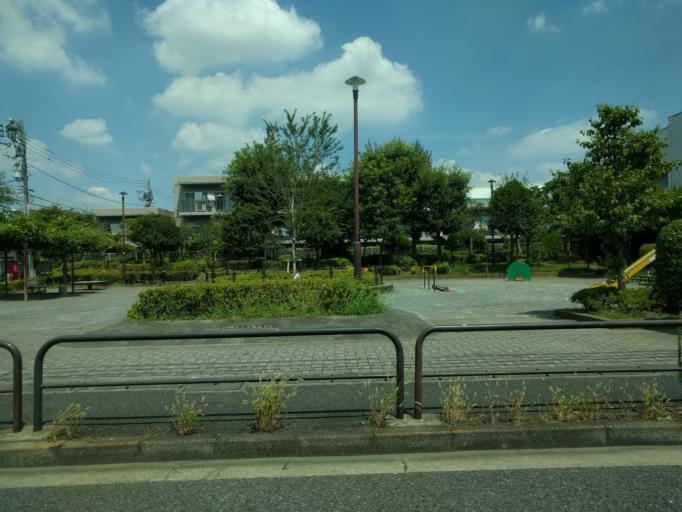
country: JP
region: Tokyo
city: Tokyo
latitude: 35.6301
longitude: 139.6294
